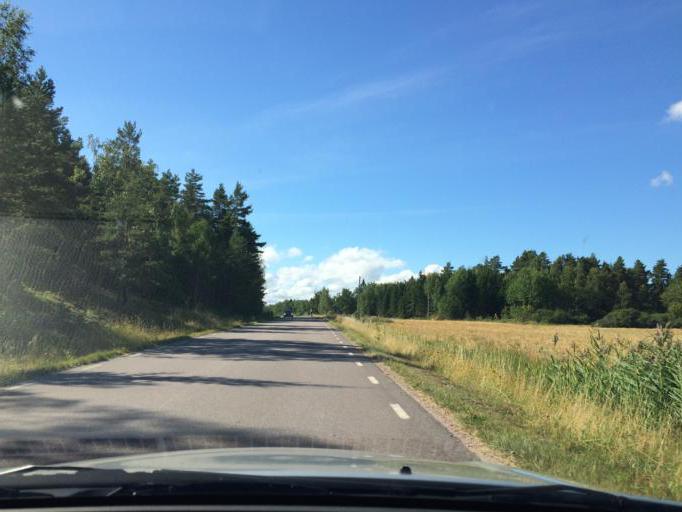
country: SE
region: Soedermanland
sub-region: Eskilstuna Kommun
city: Torshalla
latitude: 59.5222
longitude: 16.4385
